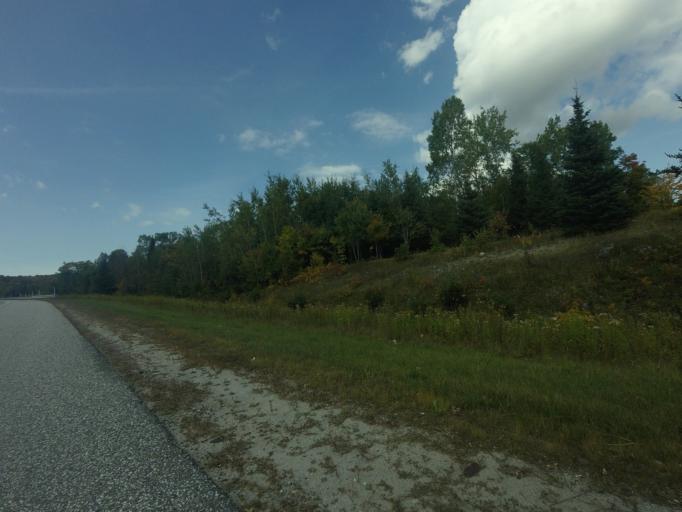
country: CA
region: Quebec
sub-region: Laurentides
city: Mont-Laurier
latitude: 46.5624
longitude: -75.6828
